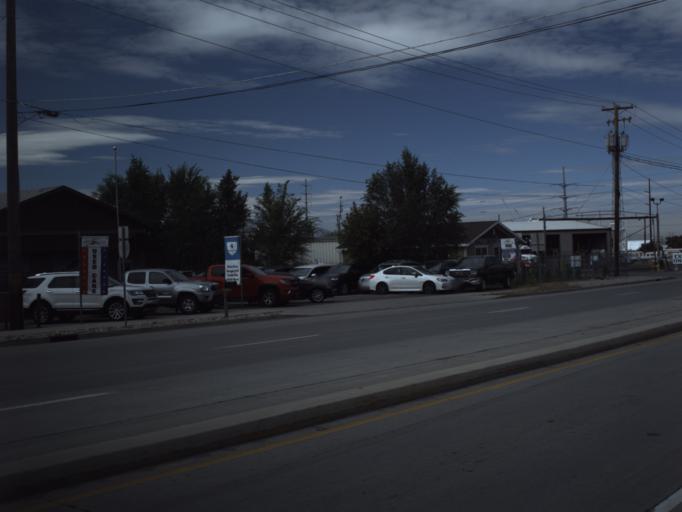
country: US
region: Utah
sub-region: Davis County
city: West Bountiful
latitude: 40.8843
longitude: -111.8996
